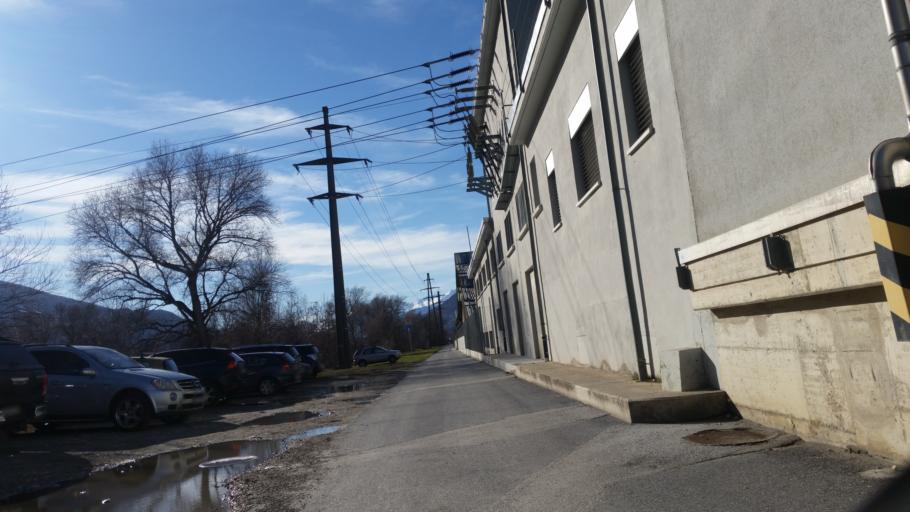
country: CH
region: Valais
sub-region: Sierre District
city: Sierre
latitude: 46.2811
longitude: 7.5303
